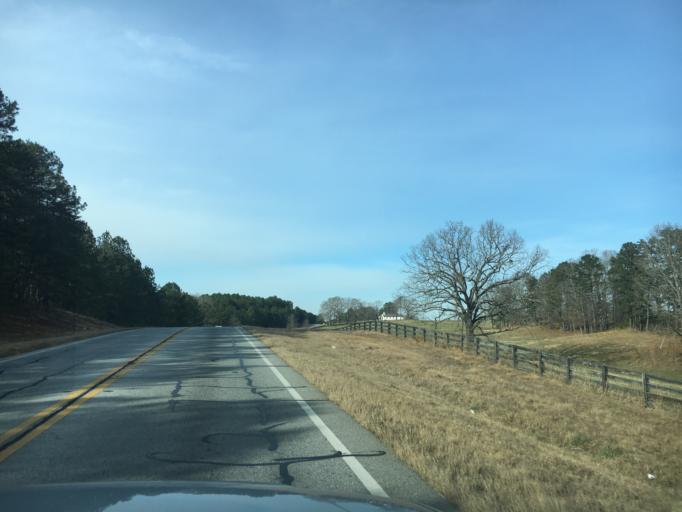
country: US
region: Georgia
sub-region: Jackson County
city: Hoschton
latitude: 34.0765
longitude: -83.7398
